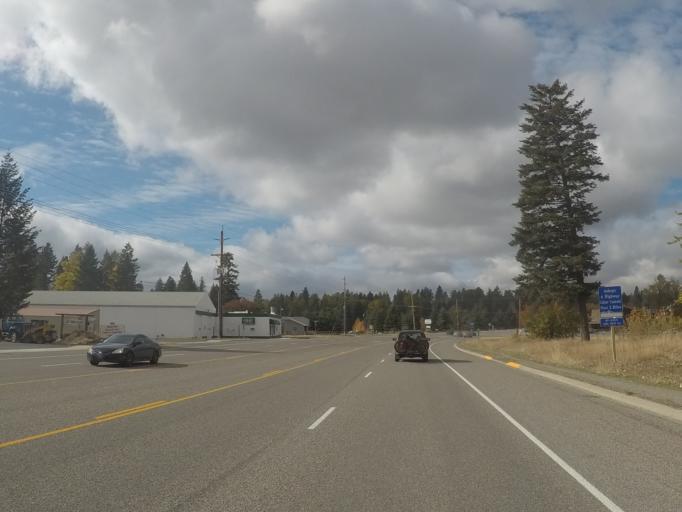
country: US
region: Montana
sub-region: Flathead County
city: Columbia Falls
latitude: 48.3669
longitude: -114.1732
